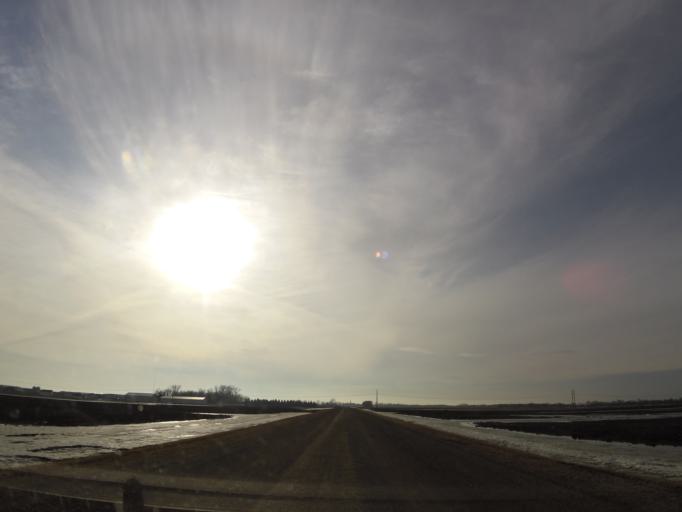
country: US
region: North Dakota
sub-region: Walsh County
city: Grafton
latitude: 48.4265
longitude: -97.2599
